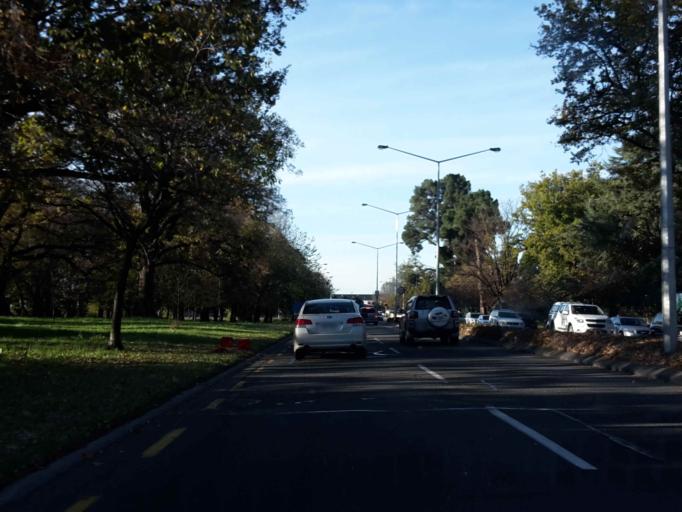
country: NZ
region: Canterbury
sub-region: Christchurch City
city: Christchurch
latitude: -43.5224
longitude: 172.6234
